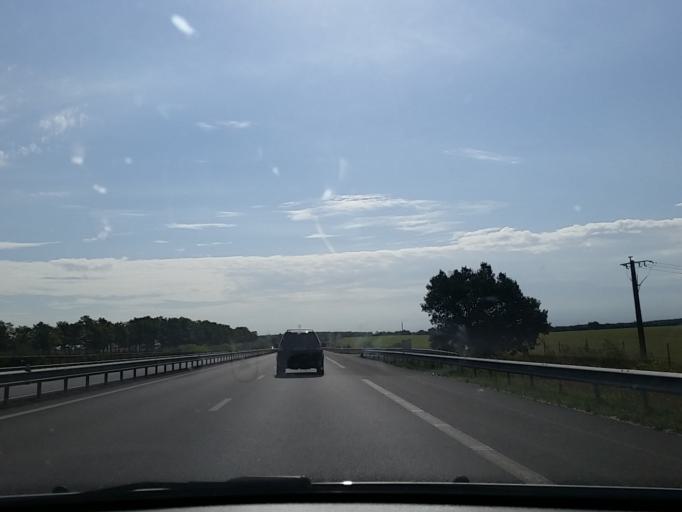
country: FR
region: Centre
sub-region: Departement du Cher
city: Trouy
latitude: 47.0402
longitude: 2.3503
